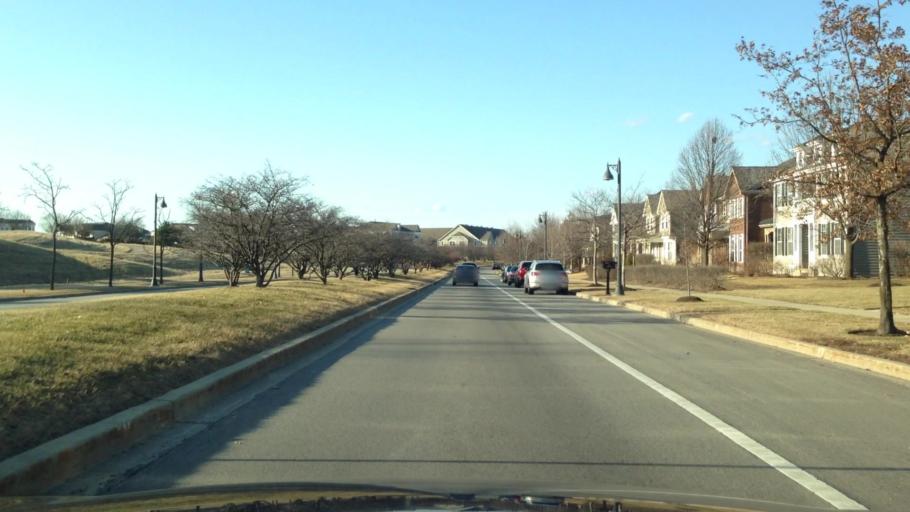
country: US
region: Illinois
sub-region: Cook County
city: Glenview
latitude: 42.0825
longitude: -87.8200
